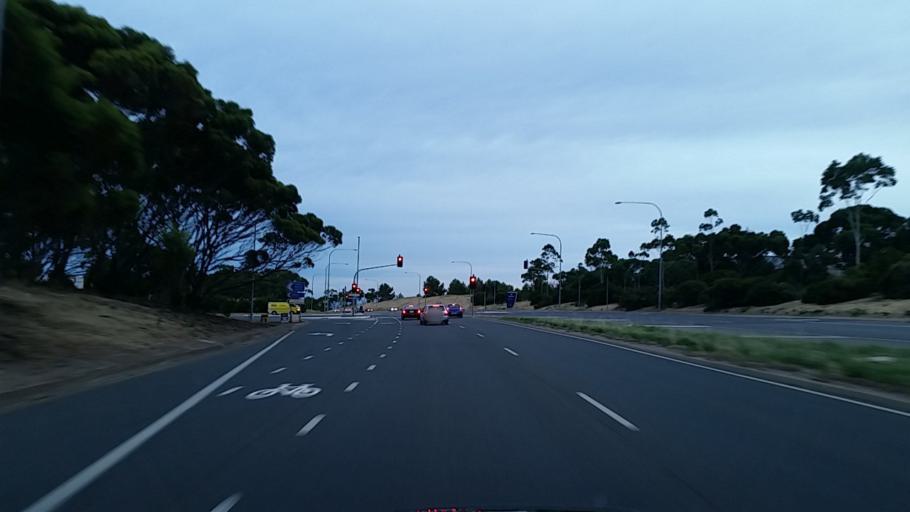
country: AU
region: South Australia
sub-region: Onkaparinga
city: Reynella
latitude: -35.1030
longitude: 138.4998
